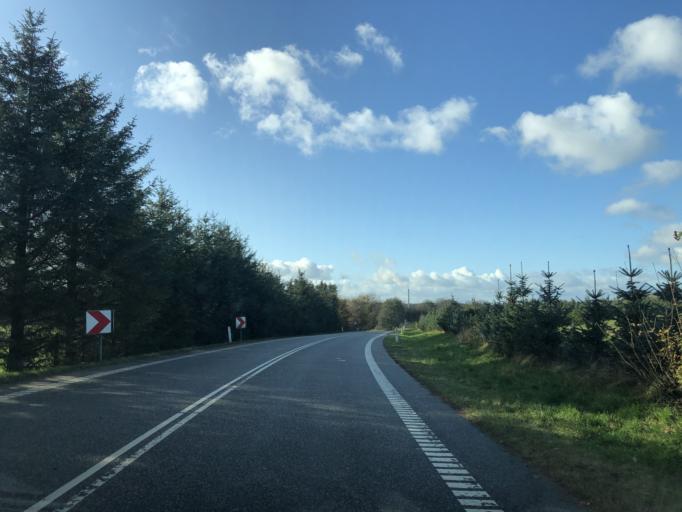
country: DK
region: Central Jutland
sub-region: Silkeborg Kommune
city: Silkeborg
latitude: 56.1418
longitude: 9.4259
